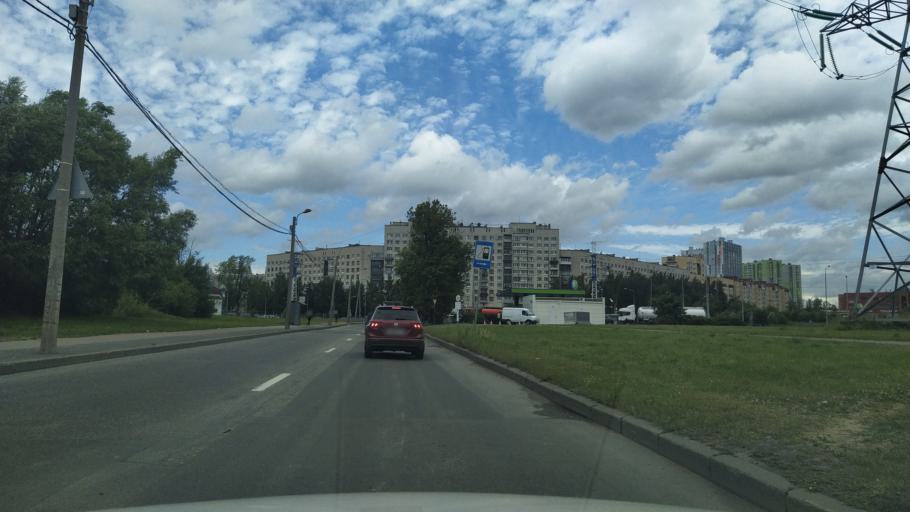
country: RU
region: Leningrad
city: Kalininskiy
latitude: 59.9778
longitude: 30.3826
